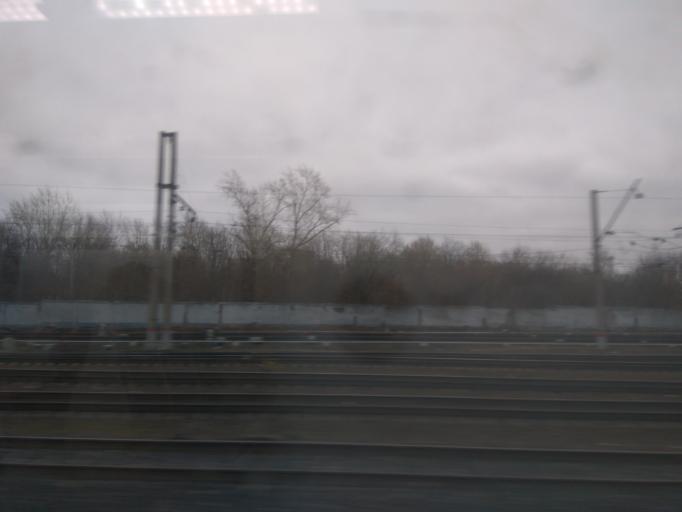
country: RU
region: Moscow
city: Lyublino
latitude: 55.6826
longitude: 37.7327
